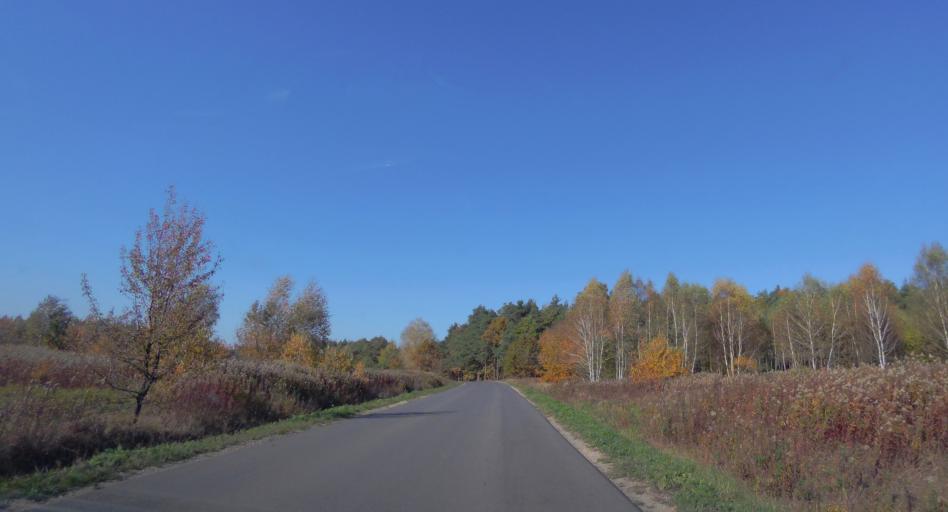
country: PL
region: Subcarpathian Voivodeship
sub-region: Powiat lezajski
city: Wola Zarczycka
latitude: 50.2880
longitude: 22.2664
